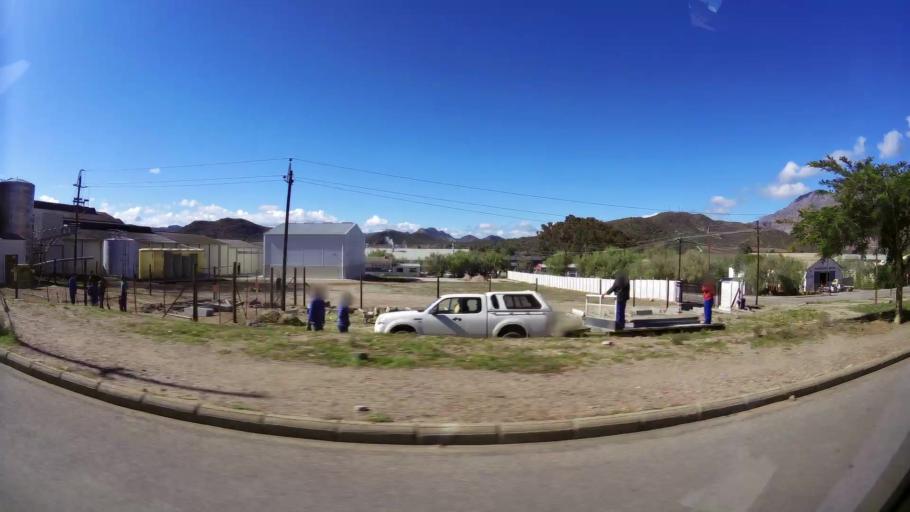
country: ZA
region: Western Cape
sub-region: Cape Winelands District Municipality
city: Ashton
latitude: -33.7780
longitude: 20.1311
